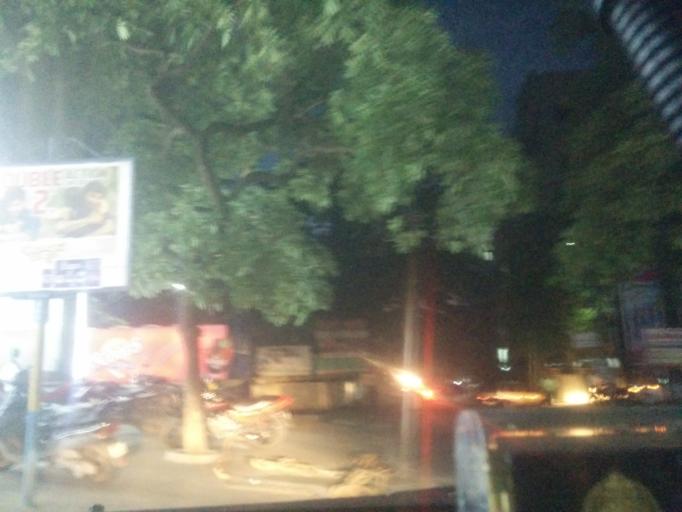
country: IN
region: Andhra Pradesh
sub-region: East Godavari
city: Rajahmundry
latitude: 17.0073
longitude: 81.7880
